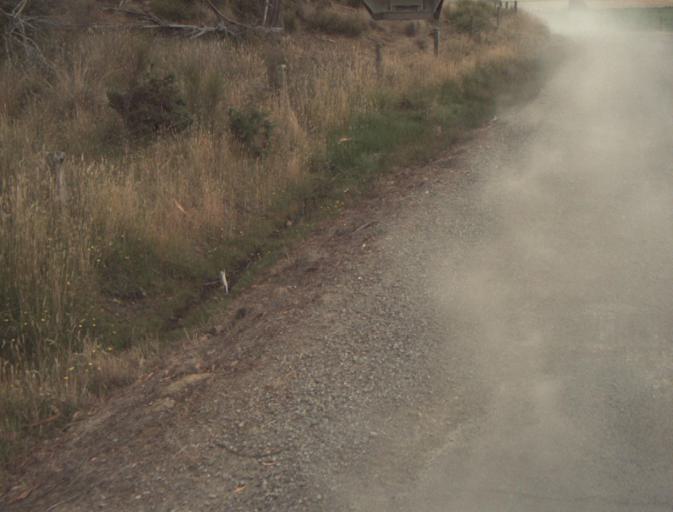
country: AU
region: Tasmania
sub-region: Northern Midlands
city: Evandale
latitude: -41.4852
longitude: 147.4401
